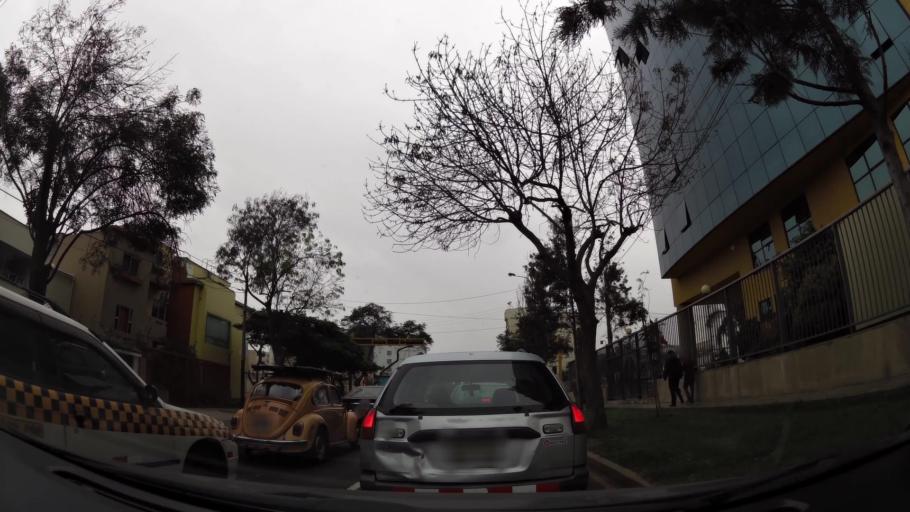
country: PE
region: Lima
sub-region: Lima
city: San Isidro
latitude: -12.0935
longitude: -77.0385
